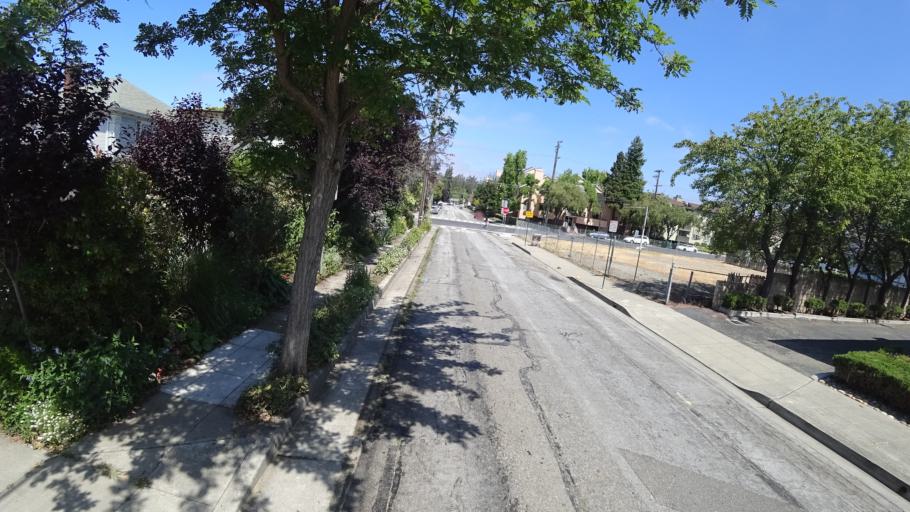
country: US
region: California
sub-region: Alameda County
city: Hayward
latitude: 37.6760
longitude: -122.0774
